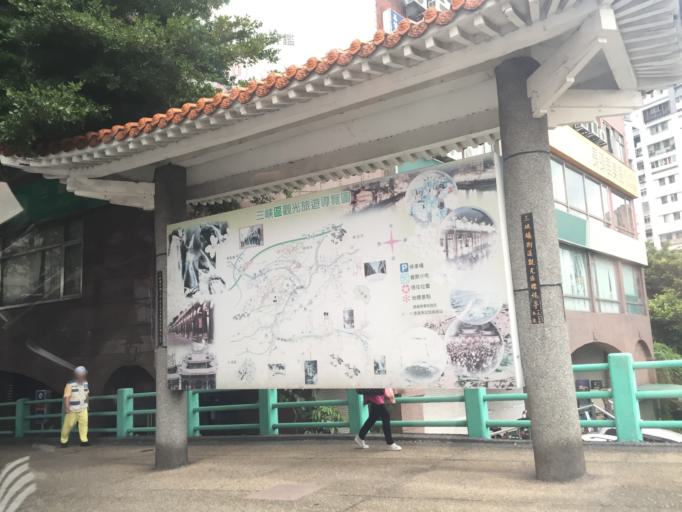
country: TW
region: Taiwan
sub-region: Taoyuan
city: Taoyuan
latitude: 24.9353
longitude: 121.3747
